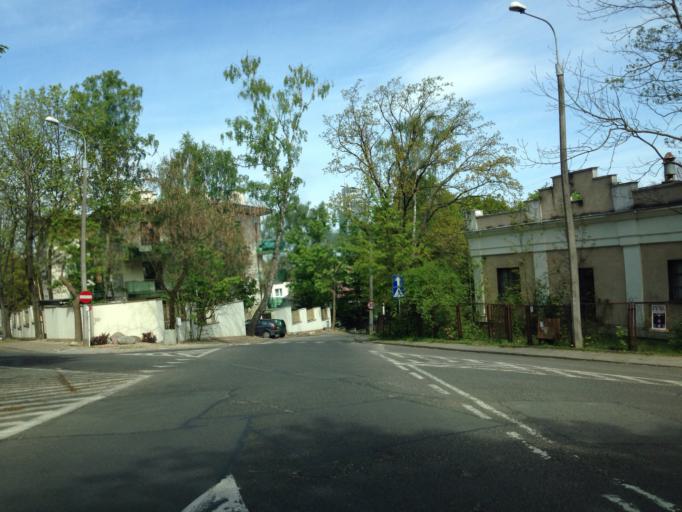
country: PL
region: Pomeranian Voivodeship
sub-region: Gdynia
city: Gdynia
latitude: 54.5140
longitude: 18.5471
